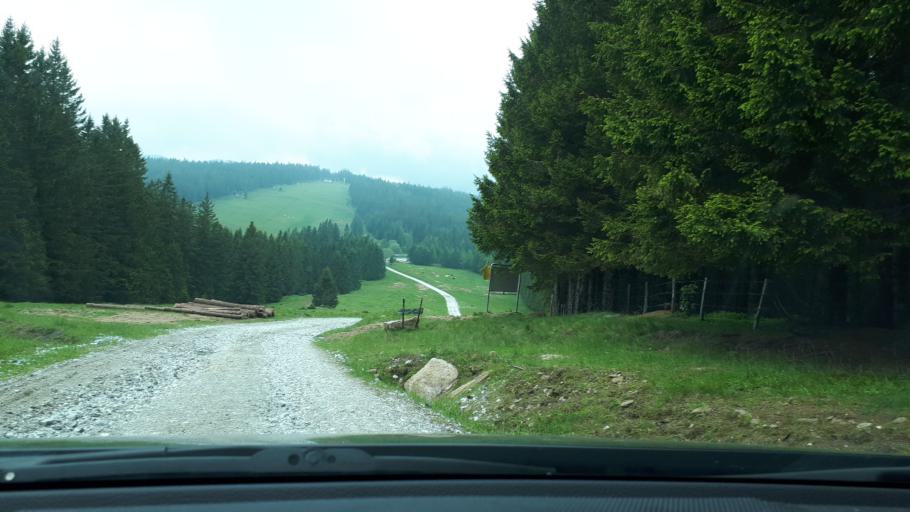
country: AT
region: Styria
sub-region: Politischer Bezirk Voitsberg
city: Modriach
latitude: 46.9121
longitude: 15.0430
